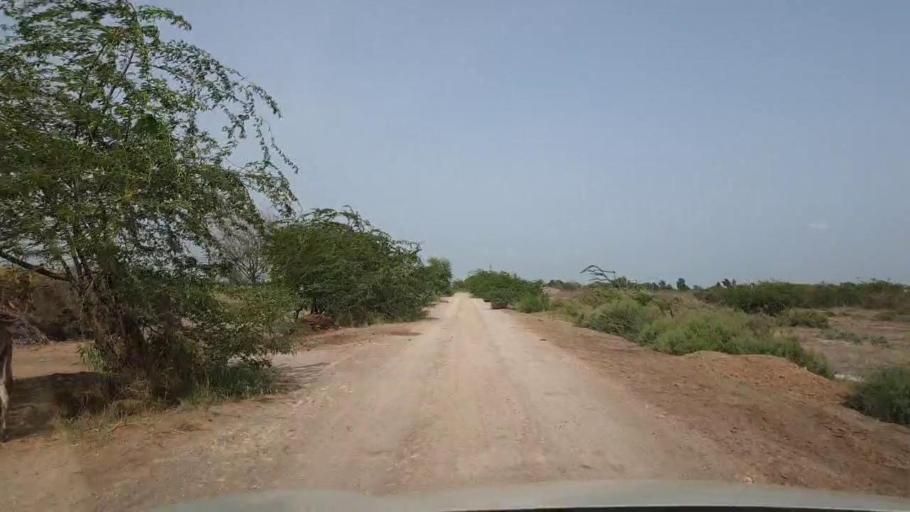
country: PK
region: Sindh
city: Mirwah Gorchani
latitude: 25.2778
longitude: 68.9545
